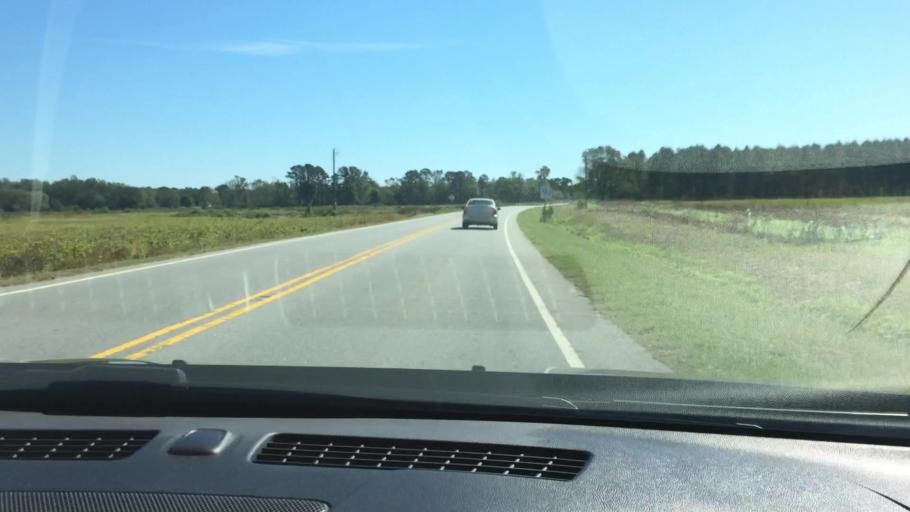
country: US
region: North Carolina
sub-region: Pitt County
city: Grifton
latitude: 35.3500
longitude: -77.3274
